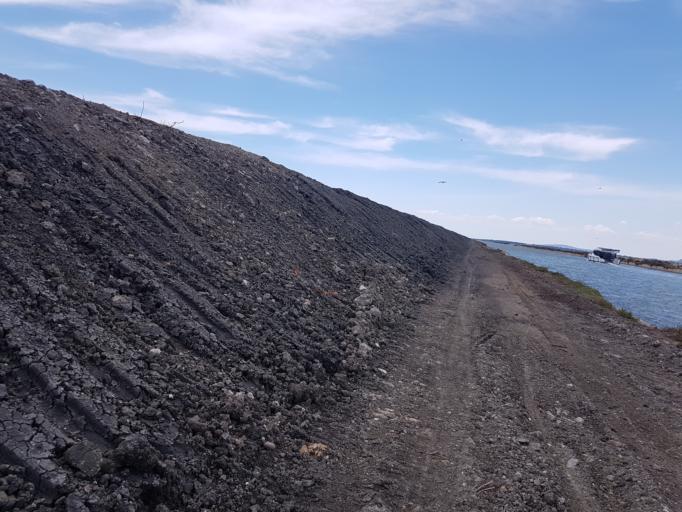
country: FR
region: Languedoc-Roussillon
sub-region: Departement de l'Herault
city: Villeneuve-les-Maguelone
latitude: 43.5047
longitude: 3.8645
